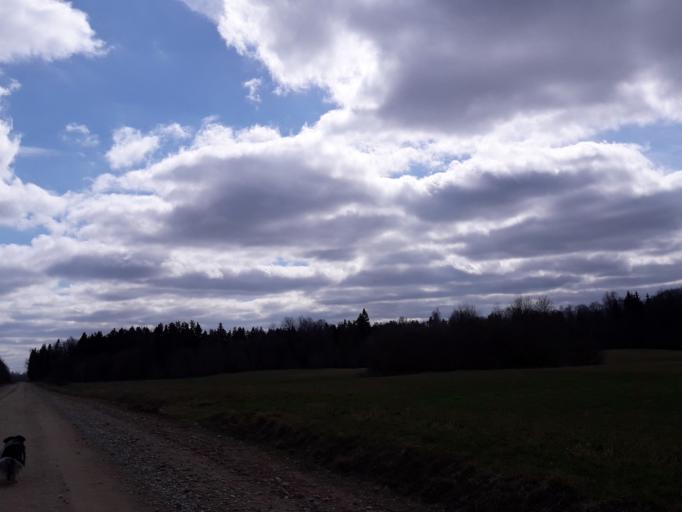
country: LV
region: Talsu Rajons
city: Sabile
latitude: 56.9114
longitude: 22.3986
